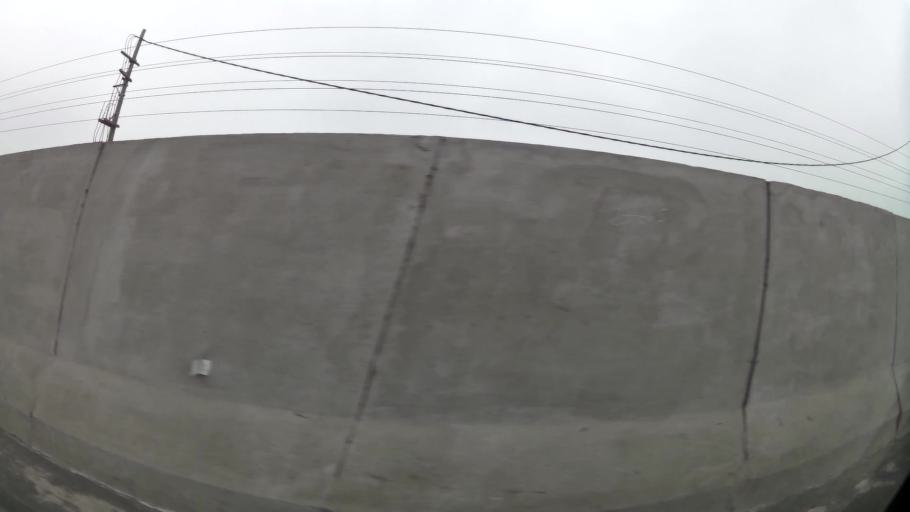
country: PE
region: Lima
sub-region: Lima
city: Urb. Santo Domingo
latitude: -11.9227
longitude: -77.0732
